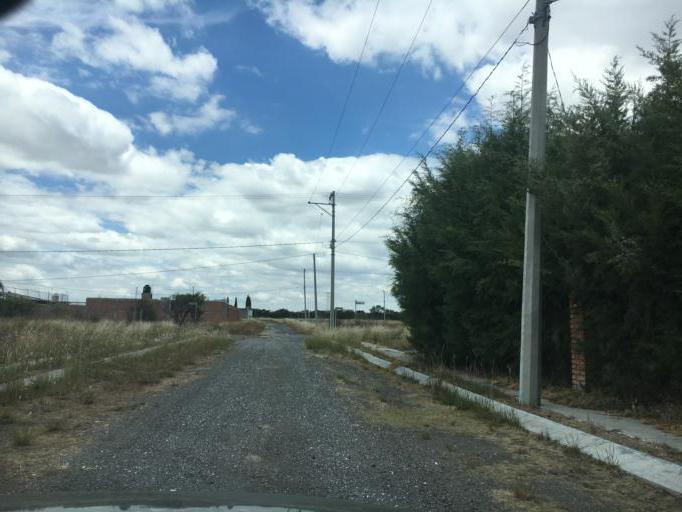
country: MX
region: Guanajuato
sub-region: San Francisco del Rincon
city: Barrio de Guadalupe del Mezquitillo
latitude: 20.9257
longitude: -101.7512
